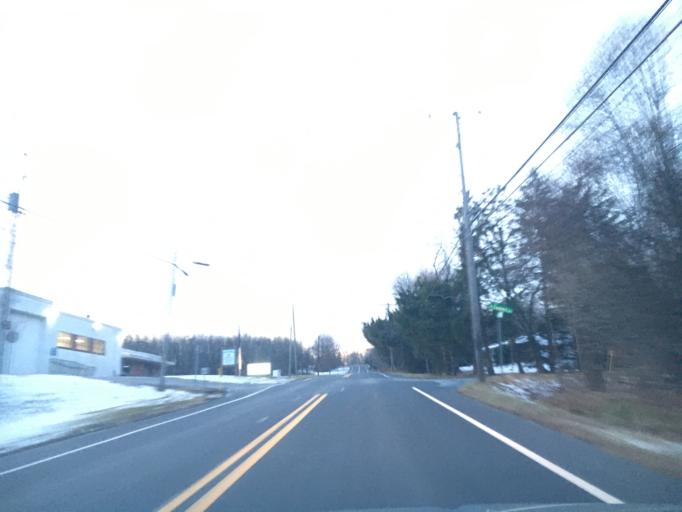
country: US
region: Pennsylvania
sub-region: Northampton County
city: Bath
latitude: 40.7814
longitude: -75.4016
